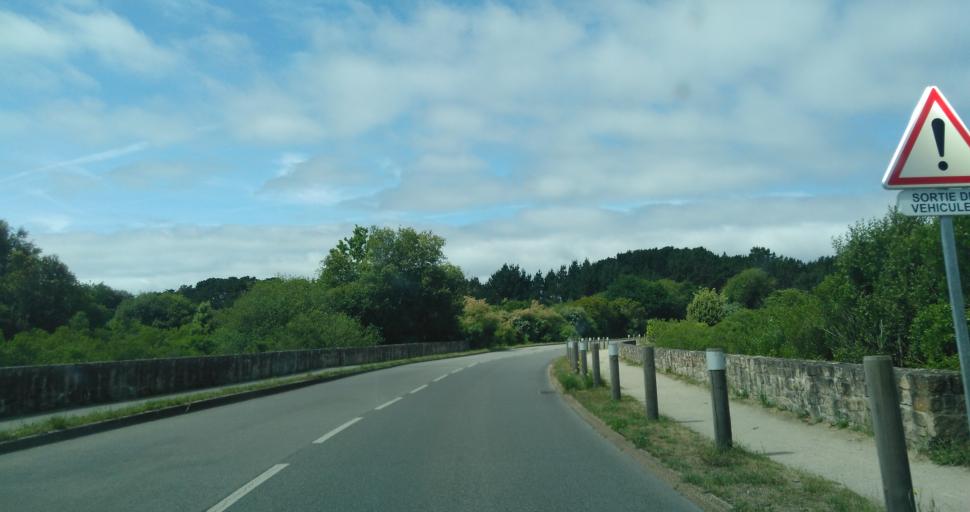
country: FR
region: Brittany
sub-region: Departement du Morbihan
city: La Trinite-sur-Mer
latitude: 47.5783
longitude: -3.0340
